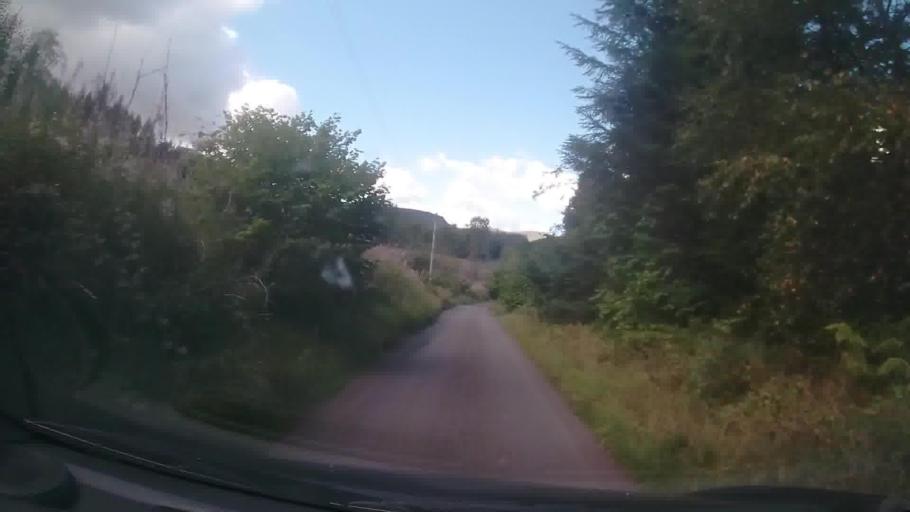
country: GB
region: Wales
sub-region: Merthyr Tydfil County Borough
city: Merthyr Tydfil
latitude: 51.8356
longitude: -3.3904
